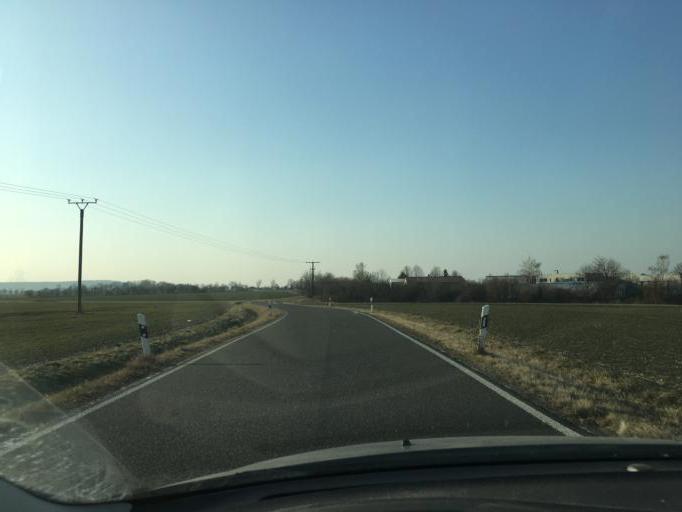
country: DE
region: Saxony
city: Kitzscher
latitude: 51.1852
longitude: 12.5753
